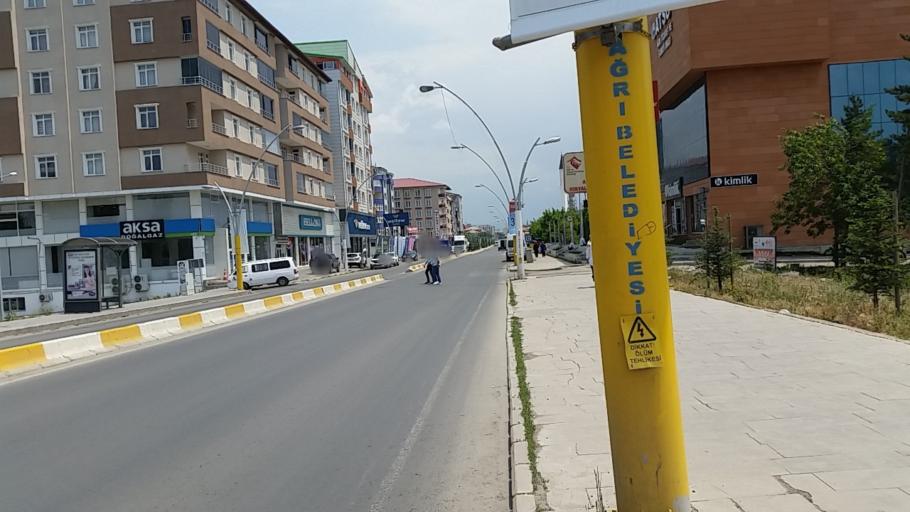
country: TR
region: Agri
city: Agri
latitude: 39.7188
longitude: 43.0297
